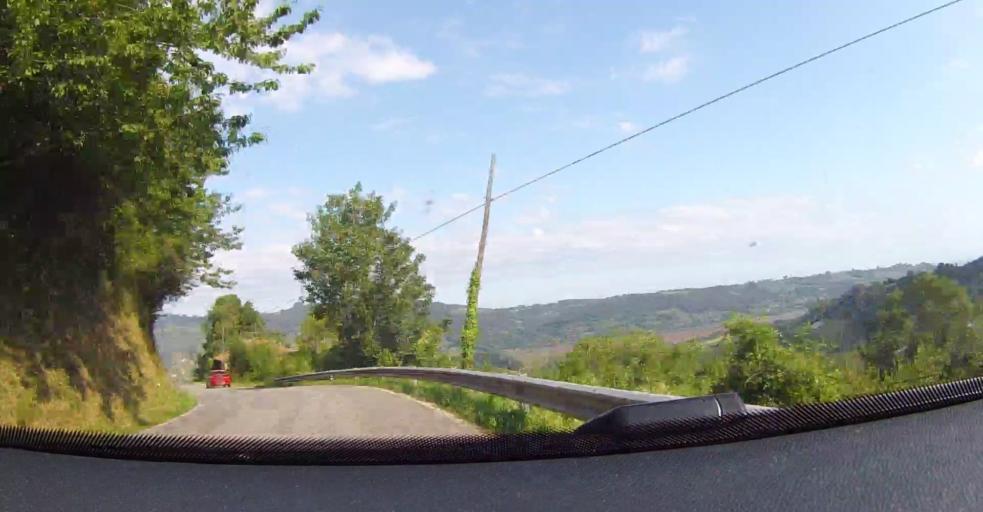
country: ES
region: Asturias
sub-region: Province of Asturias
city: Villaviciosa
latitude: 43.4854
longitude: -5.4102
